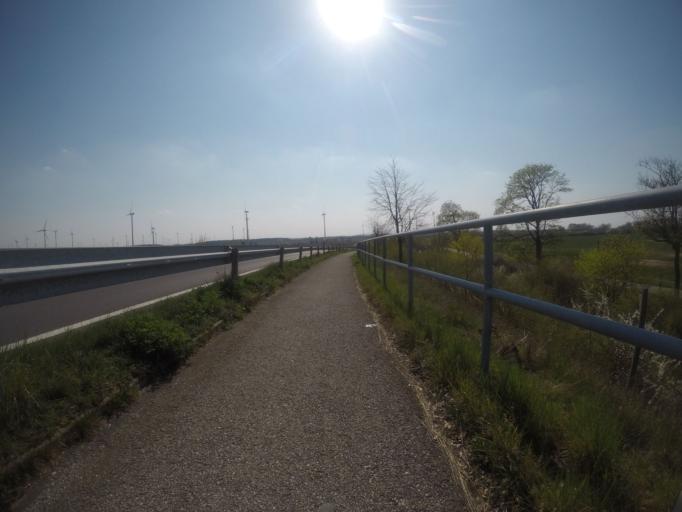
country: DE
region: Brandenburg
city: Nauen
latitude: 52.5570
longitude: 12.8693
